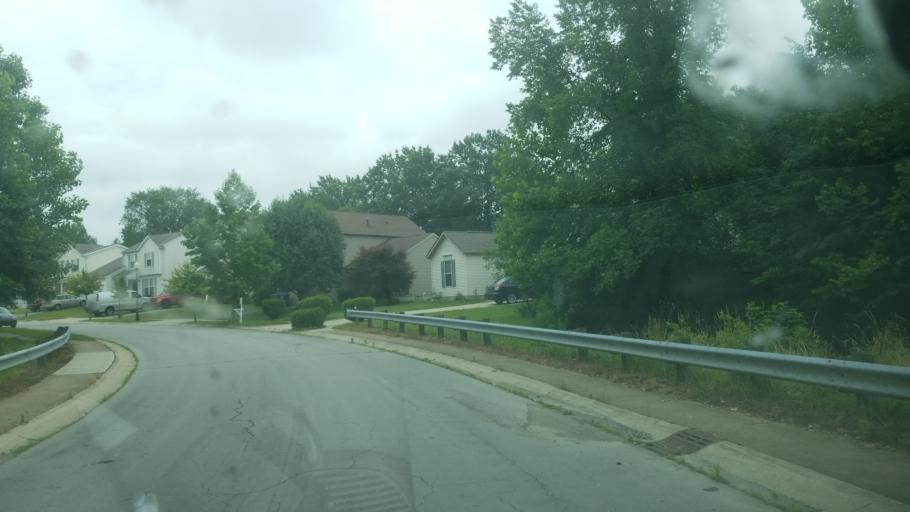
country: US
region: Ohio
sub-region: Franklin County
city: Reynoldsburg
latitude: 39.9994
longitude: -82.7859
